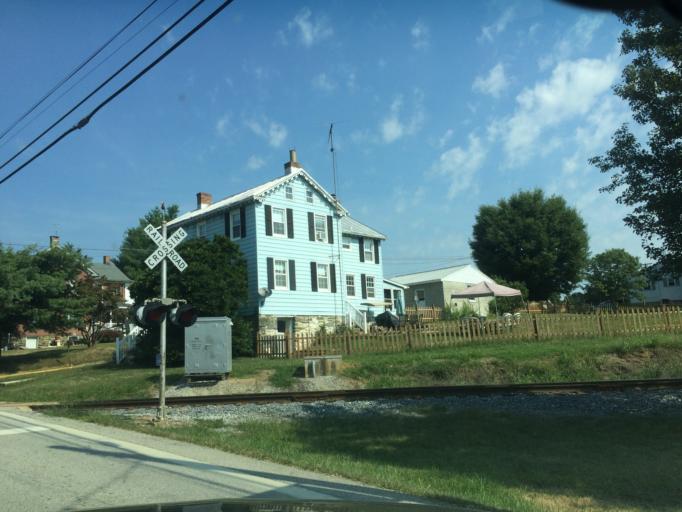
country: US
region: Maryland
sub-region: Carroll County
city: New Windsor
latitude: 39.5396
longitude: -77.1058
